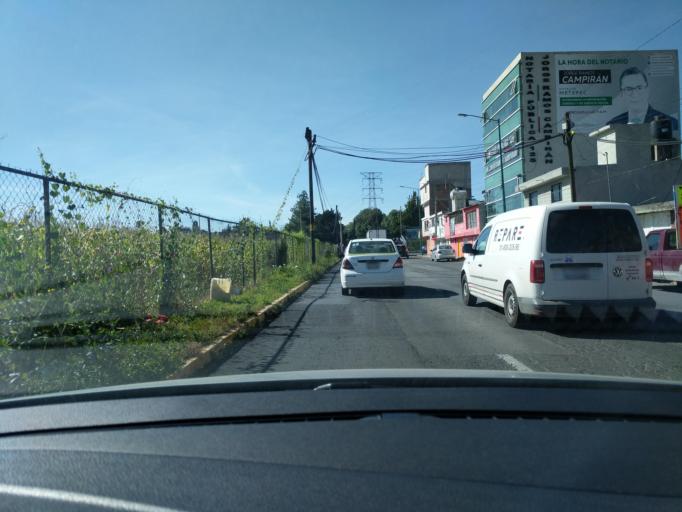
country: MX
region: Mexico
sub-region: Metepec
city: San Jorge Pueblo Nuevo
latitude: 19.2659
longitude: -99.6310
